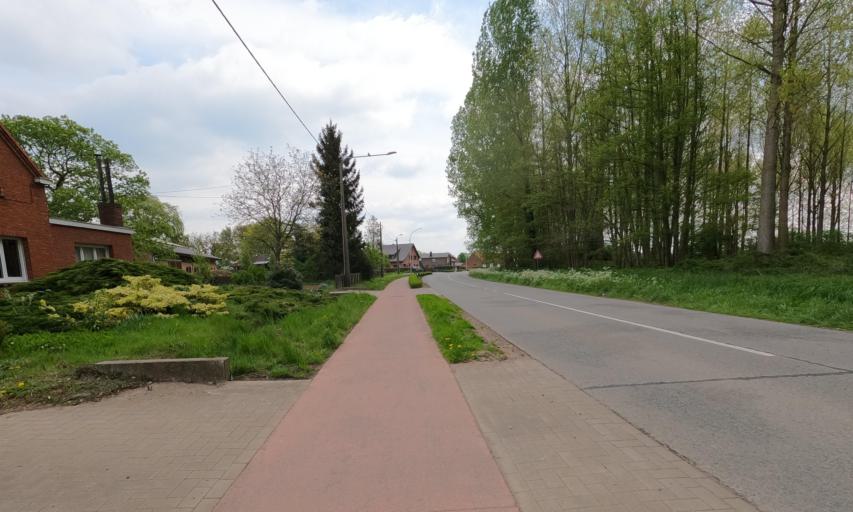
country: BE
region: Flanders
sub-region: Provincie Antwerpen
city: Zandhoven
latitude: 51.2242
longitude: 4.6822
